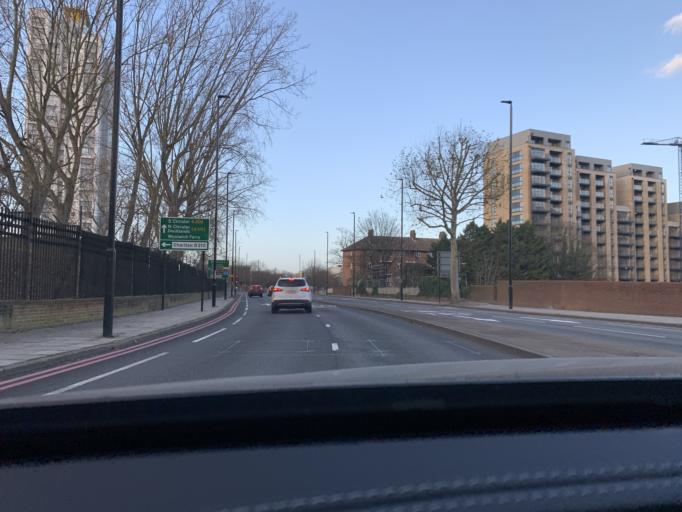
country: GB
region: England
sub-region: Greater London
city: Woolwich
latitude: 51.4874
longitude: 0.0634
